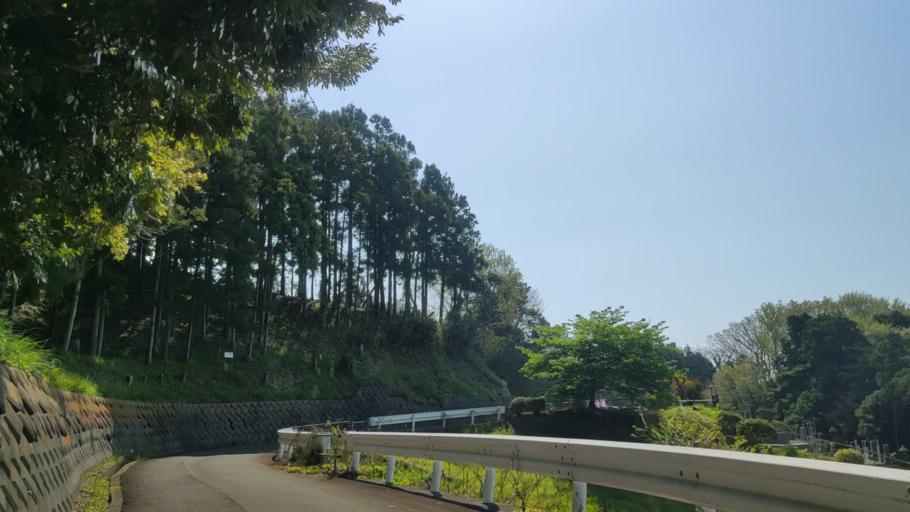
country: JP
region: Kanagawa
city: Ninomiya
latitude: 35.3254
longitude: 139.2694
